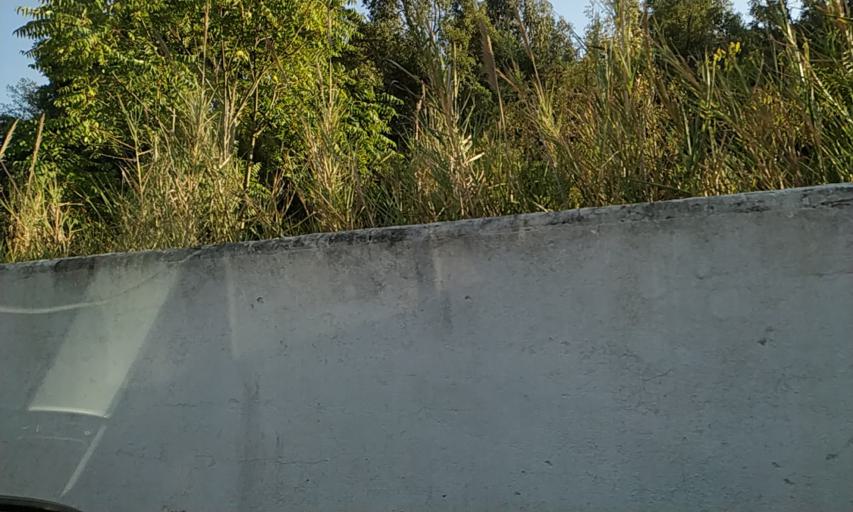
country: PT
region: Santarem
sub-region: Santarem
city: Santarem
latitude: 39.2550
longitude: -8.6738
